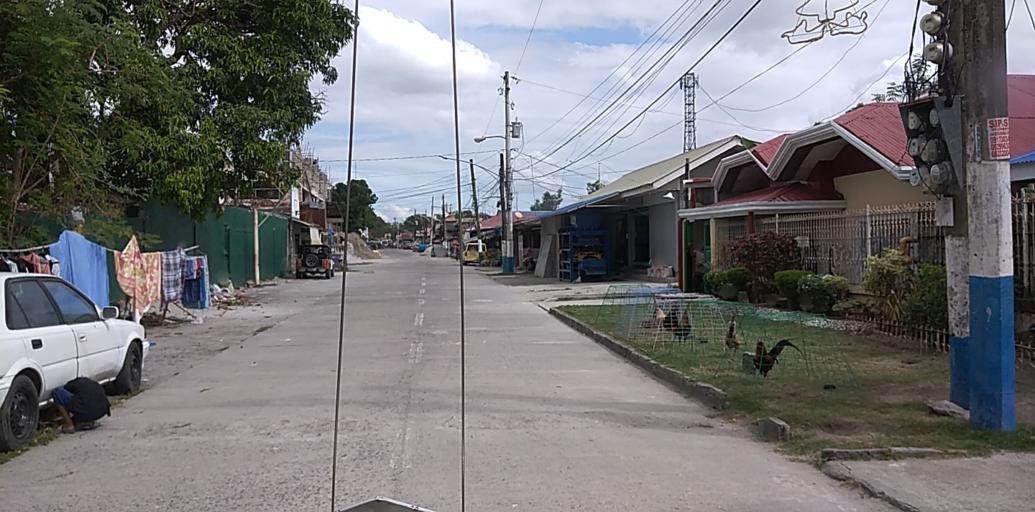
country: PH
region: Central Luzon
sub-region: Province of Pampanga
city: Porac
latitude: 15.0712
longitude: 120.5398
